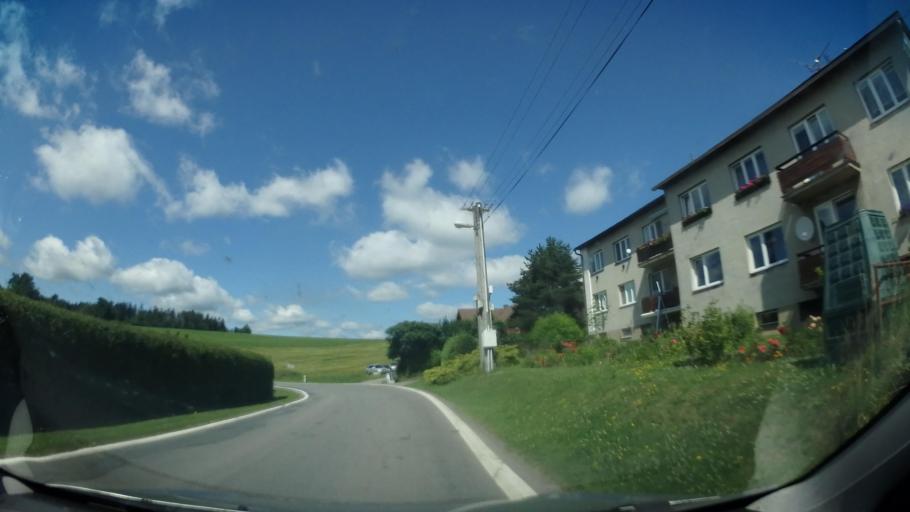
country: CZ
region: Vysocina
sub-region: Okres Zd'ar nad Sazavou
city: Nove Mesto na Morave
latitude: 49.6453
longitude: 16.1179
